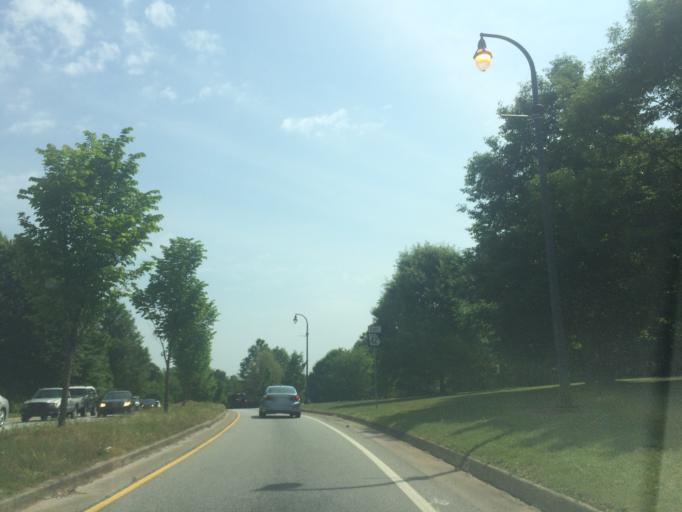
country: US
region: Georgia
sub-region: DeKalb County
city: Druid Hills
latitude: 33.7692
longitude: -84.3522
